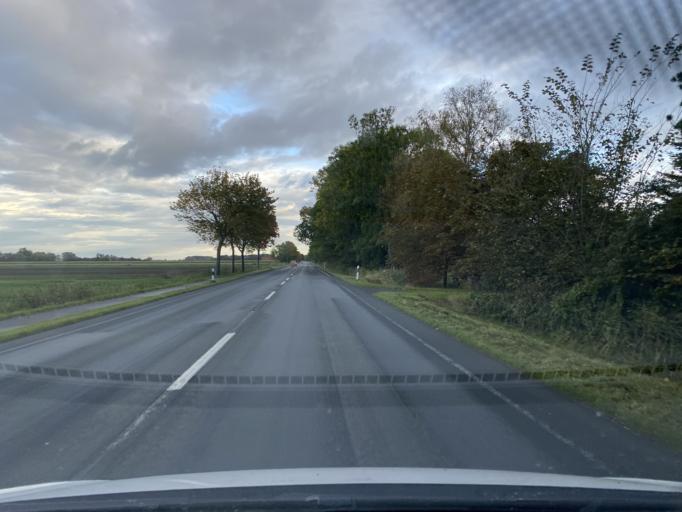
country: DE
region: Lower Saxony
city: Nordleda
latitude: 53.8035
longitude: 8.8181
